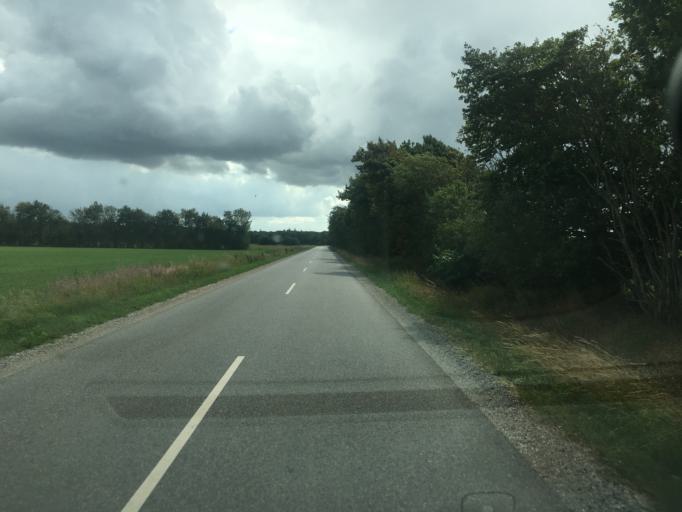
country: DK
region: South Denmark
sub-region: Tonder Kommune
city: Logumkloster
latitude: 55.0333
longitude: 8.9669
